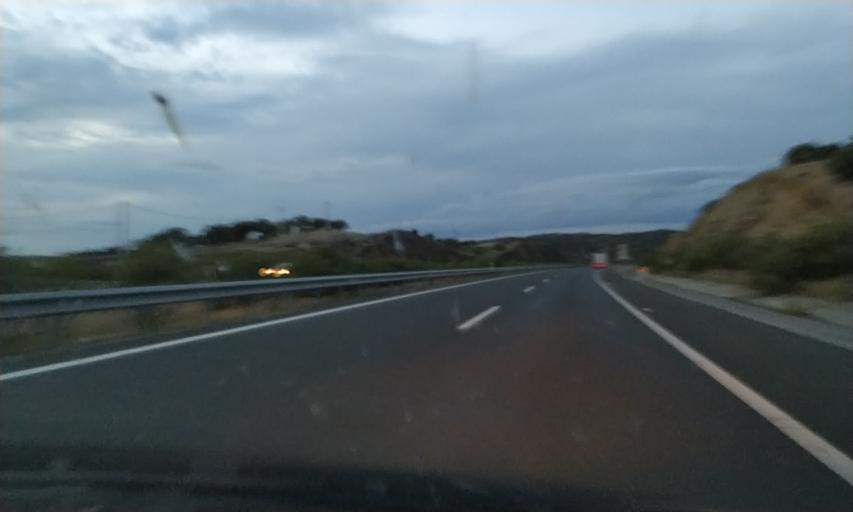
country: ES
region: Extremadura
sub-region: Provincia de Caceres
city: Santiago del Campo
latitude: 39.6081
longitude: -6.4065
